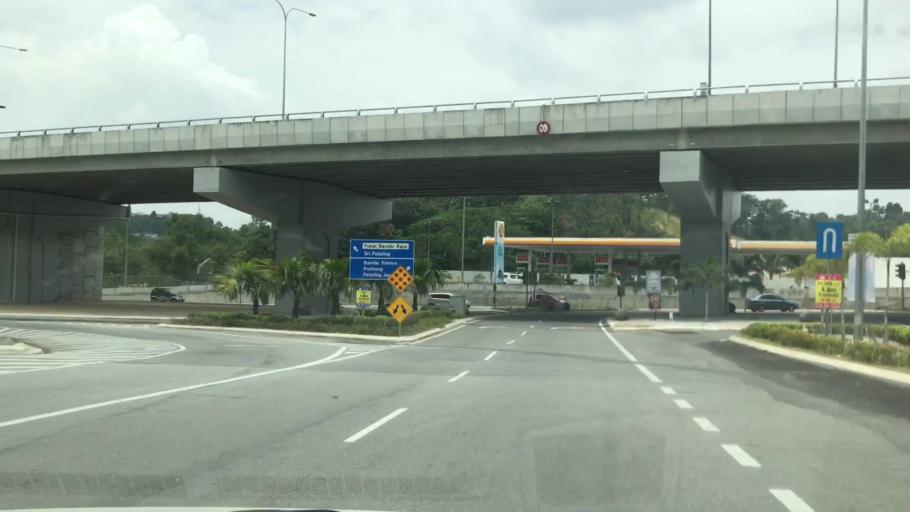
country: MY
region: Selangor
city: Kampong Baharu Balakong
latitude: 3.0503
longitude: 101.6801
